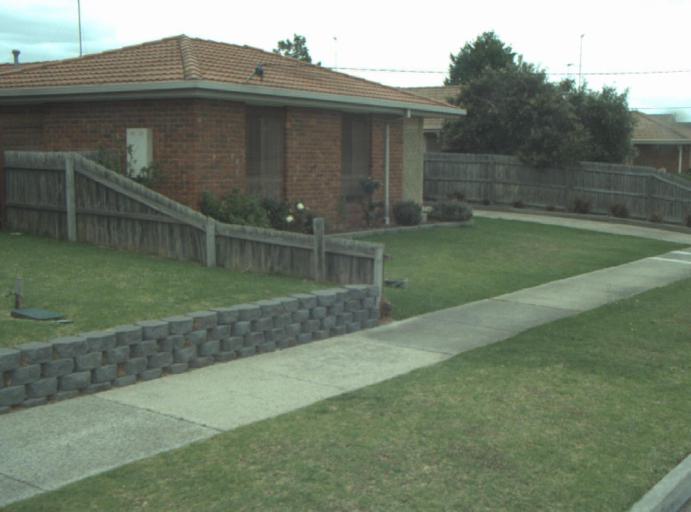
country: AU
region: Victoria
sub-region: Greater Geelong
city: Wandana Heights
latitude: -38.2008
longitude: 144.3293
